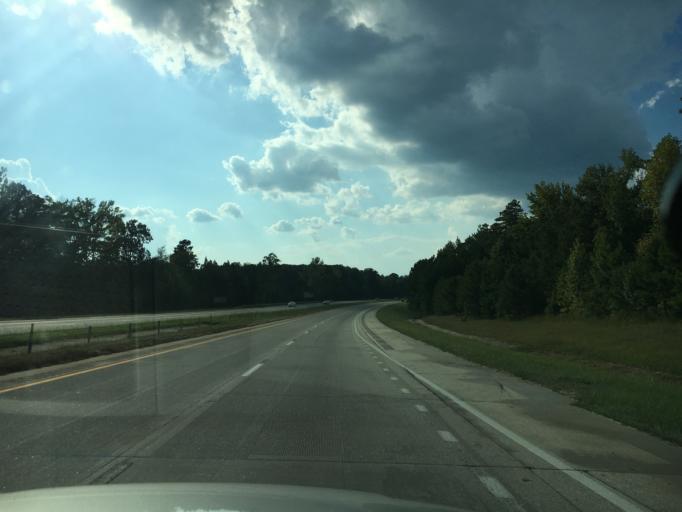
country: US
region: South Carolina
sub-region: Laurens County
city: Watts Mills
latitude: 34.5547
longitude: -82.0132
